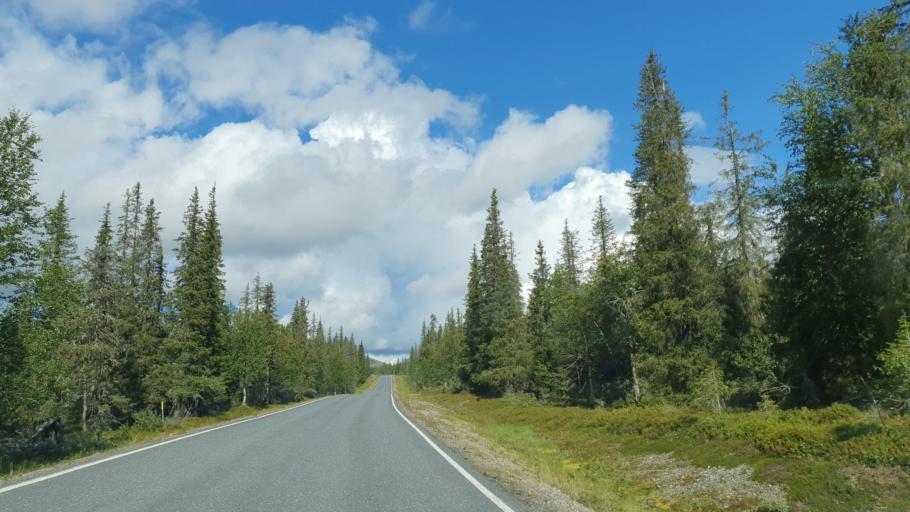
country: FI
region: Lapland
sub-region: Tunturi-Lappi
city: Muonio
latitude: 68.0374
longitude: 24.0660
